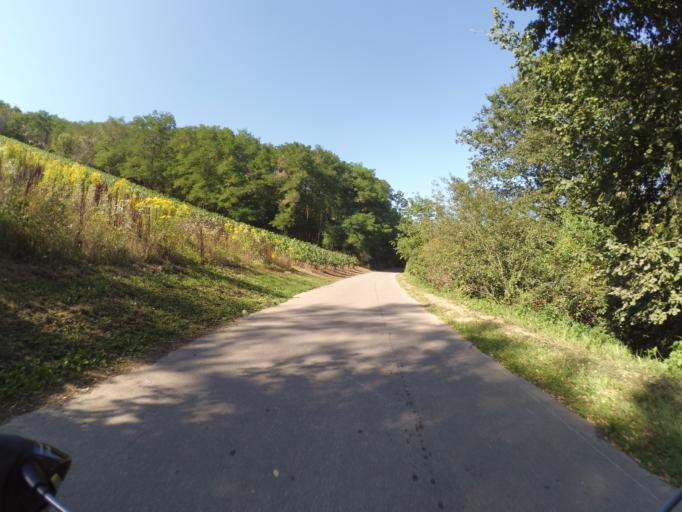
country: DE
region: Rheinland-Pfalz
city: Thornich
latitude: 49.8496
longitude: 6.8379
